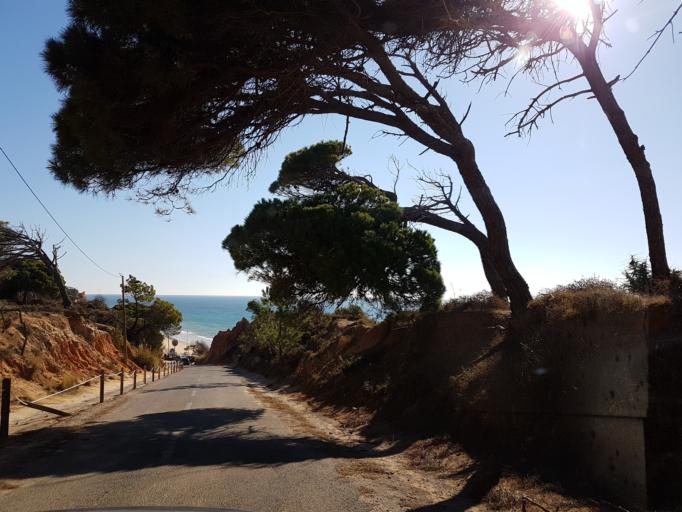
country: PT
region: Faro
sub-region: Loule
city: Boliqueime
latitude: 37.0873
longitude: -8.1695
